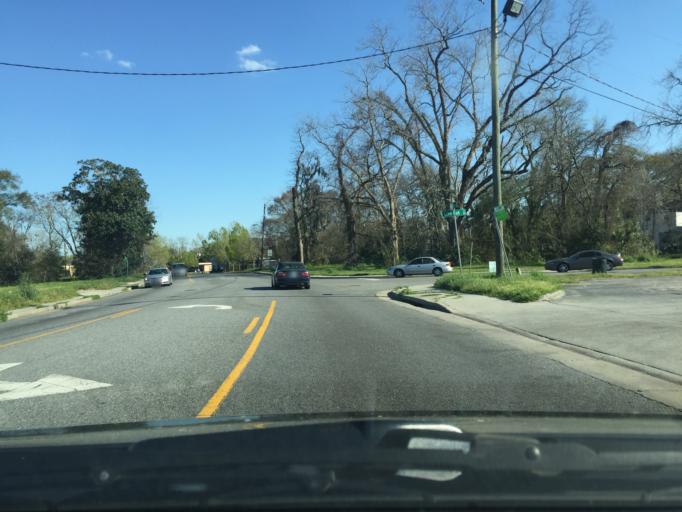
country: US
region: Georgia
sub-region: Chatham County
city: Savannah
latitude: 32.0632
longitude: -81.0781
